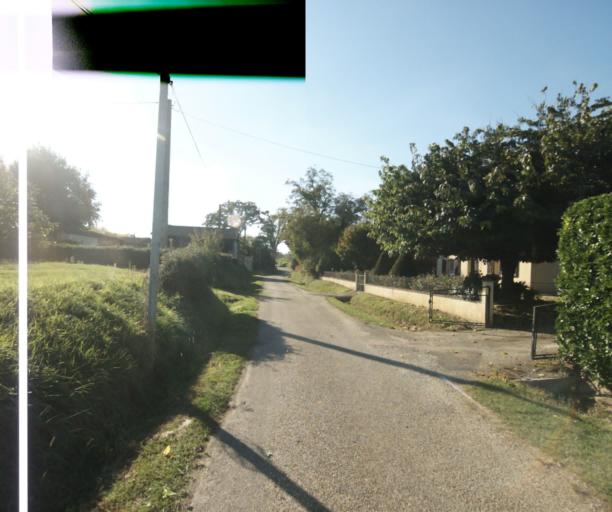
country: FR
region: Midi-Pyrenees
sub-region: Departement du Gers
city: Eauze
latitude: 43.7973
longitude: 0.1382
